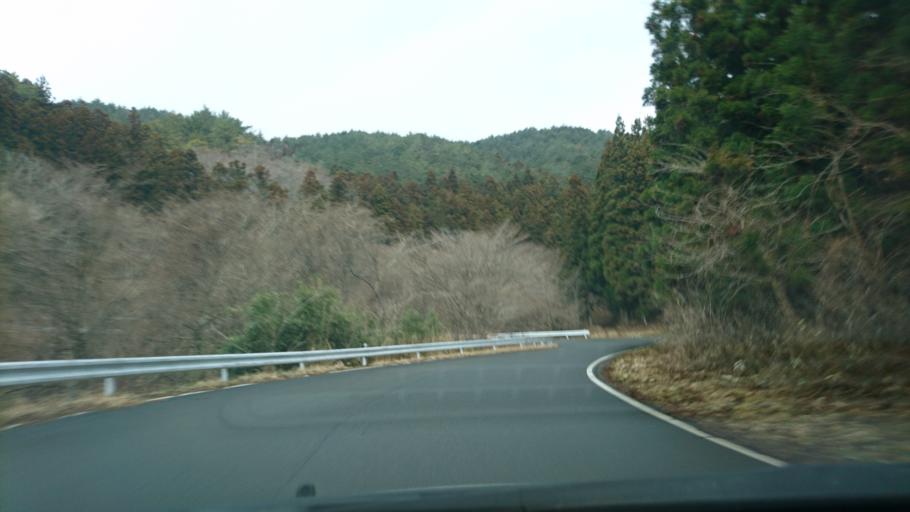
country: JP
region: Iwate
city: Ofunato
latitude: 38.9923
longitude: 141.5502
